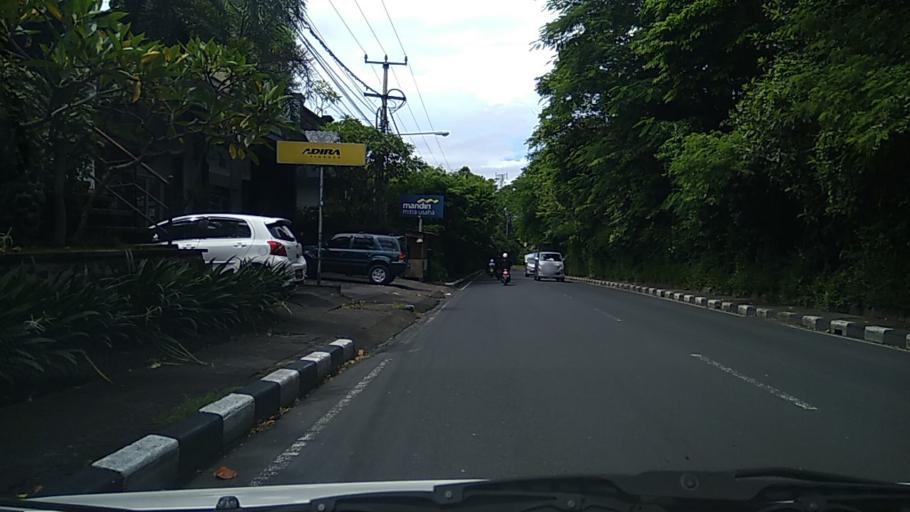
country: ID
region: Bali
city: Dajan Tangluk
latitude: -8.6441
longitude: 115.2484
